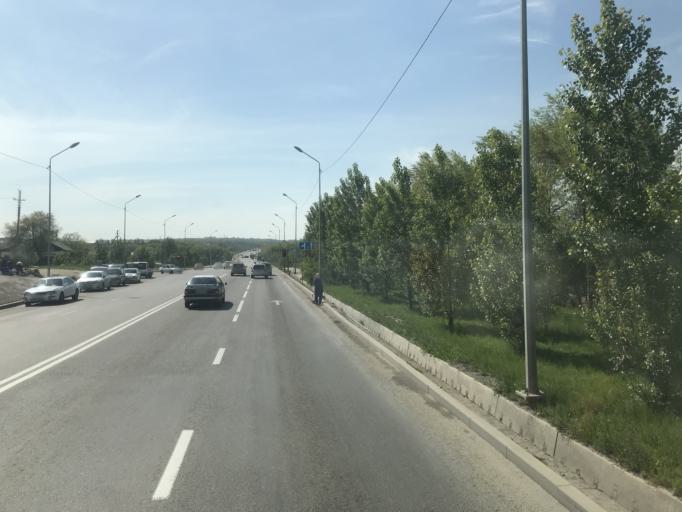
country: KZ
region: Almaty Oblysy
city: Burunday
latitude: 43.3126
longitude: 76.8548
